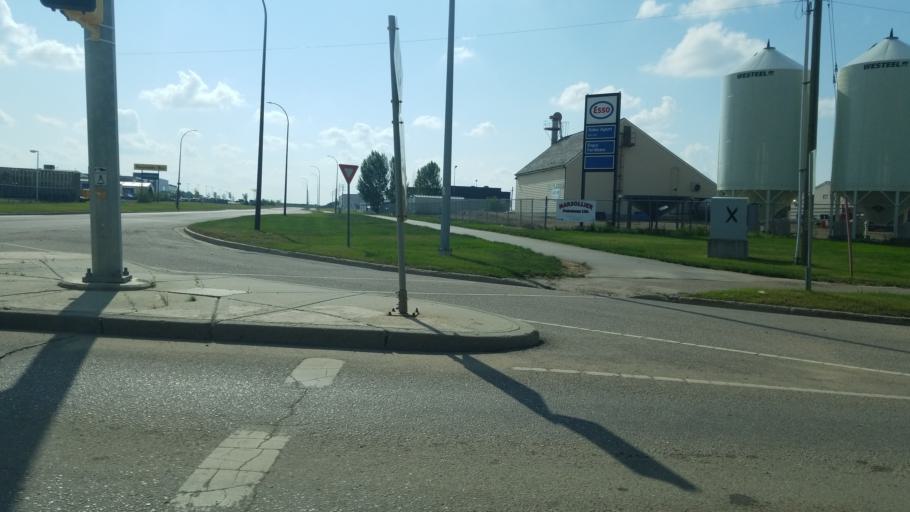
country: CA
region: Saskatchewan
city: Lloydminster
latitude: 53.2867
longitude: -110.0340
